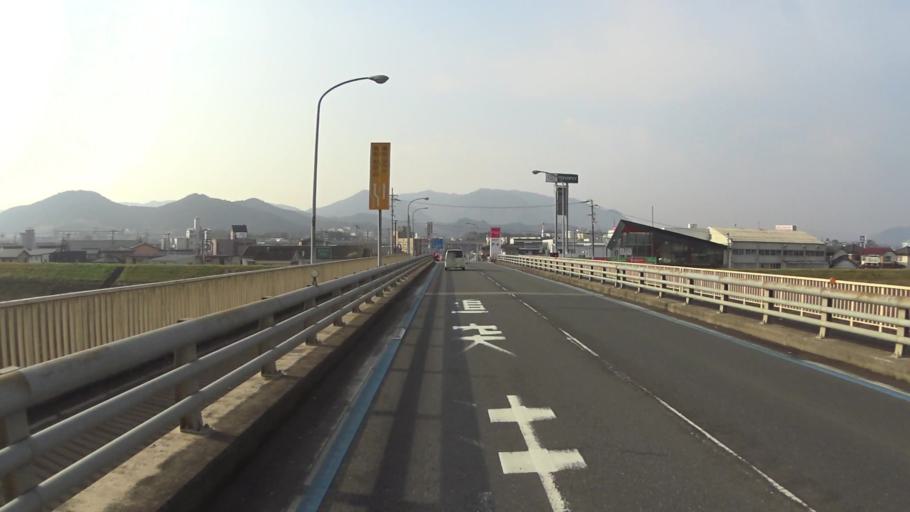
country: JP
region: Kyoto
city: Fukuchiyama
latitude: 35.2938
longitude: 135.1377
